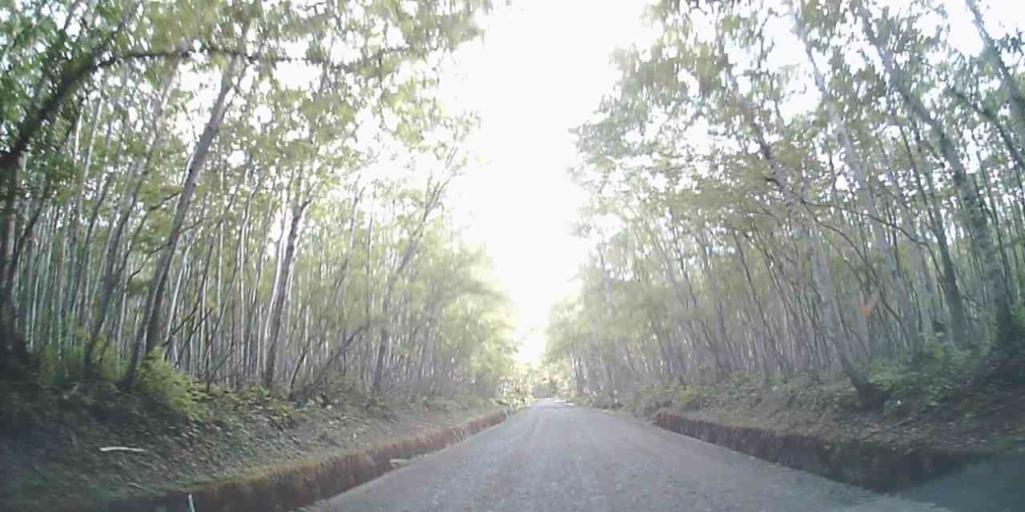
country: JP
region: Hokkaido
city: Shiraoi
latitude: 42.7066
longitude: 141.3963
